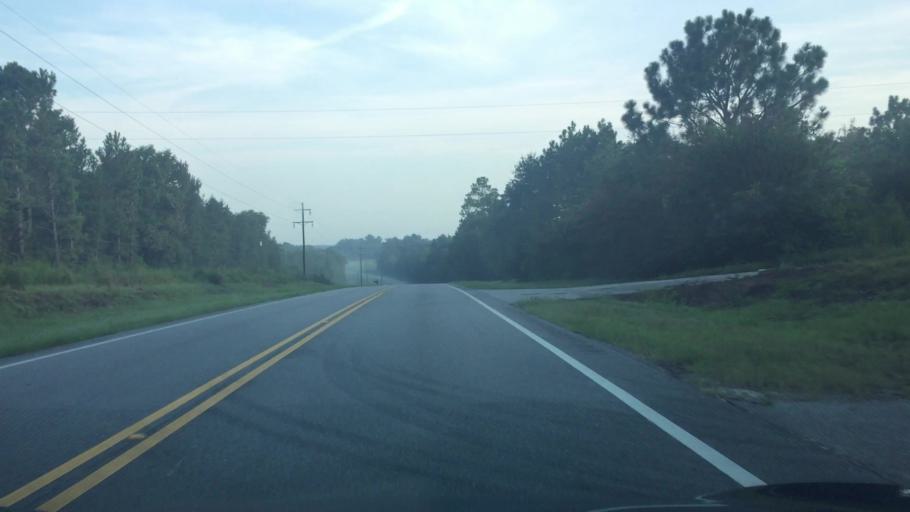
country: US
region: Alabama
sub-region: Covington County
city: Florala
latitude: 31.0693
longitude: -86.4028
